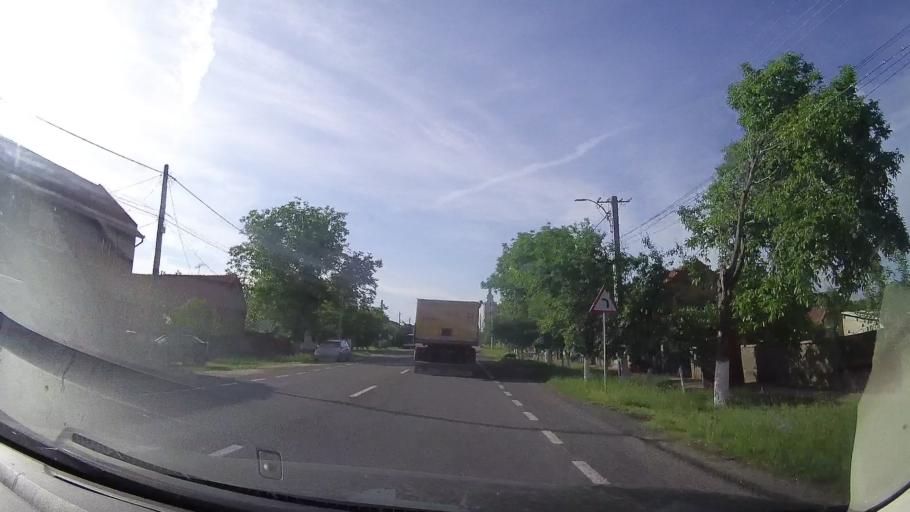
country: RO
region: Timis
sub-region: Comuna Costeiu
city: Costeiu
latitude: 45.7315
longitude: 21.8671
